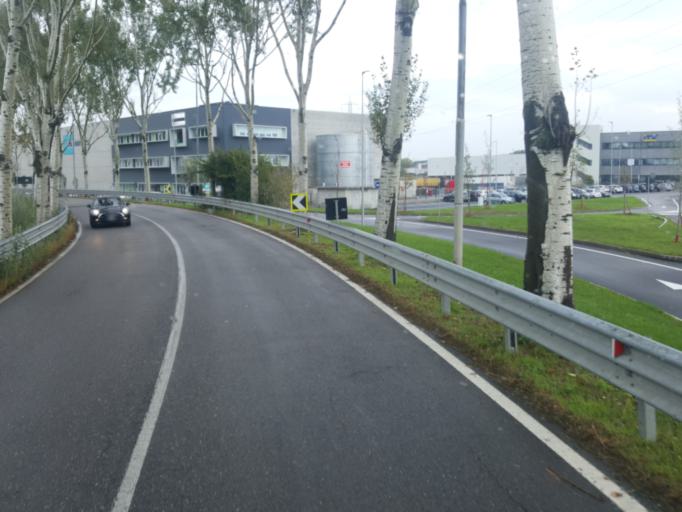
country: IT
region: Lombardy
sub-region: Provincia di Varese
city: Origgio
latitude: 45.5898
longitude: 9.0259
